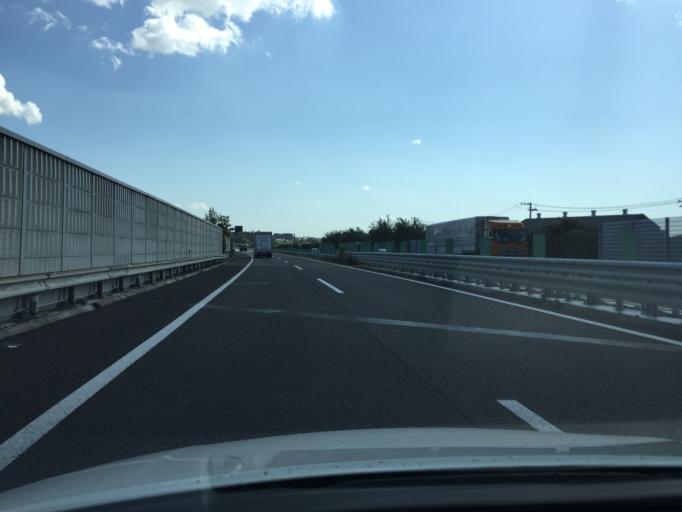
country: JP
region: Fukushima
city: Koriyama
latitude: 37.3600
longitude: 140.3146
